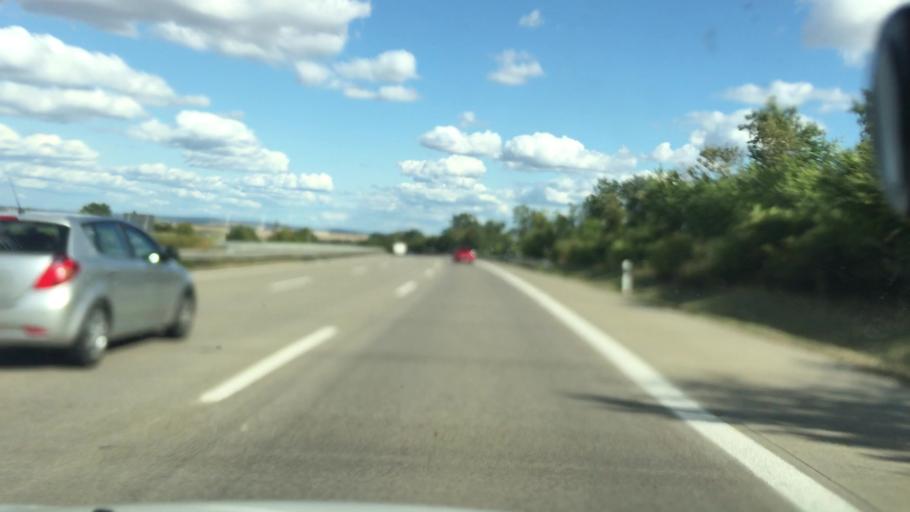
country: DE
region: Thuringia
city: Heyersdorf
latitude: 50.8365
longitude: 12.3672
